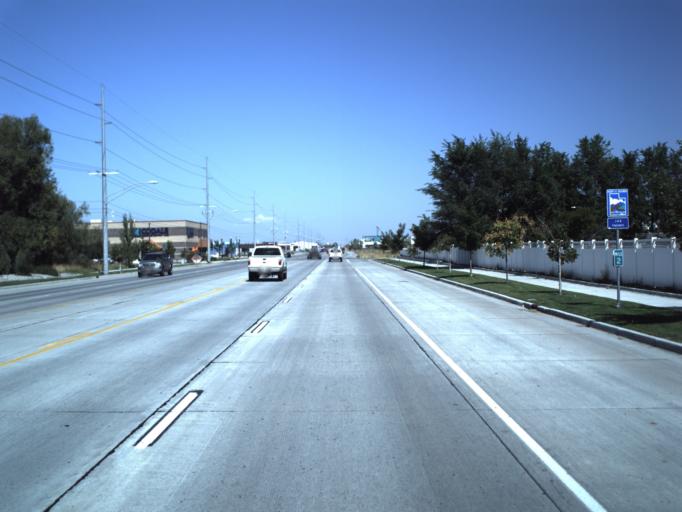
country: US
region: Utah
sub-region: Cache County
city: Logan
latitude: 41.7265
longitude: -111.8599
